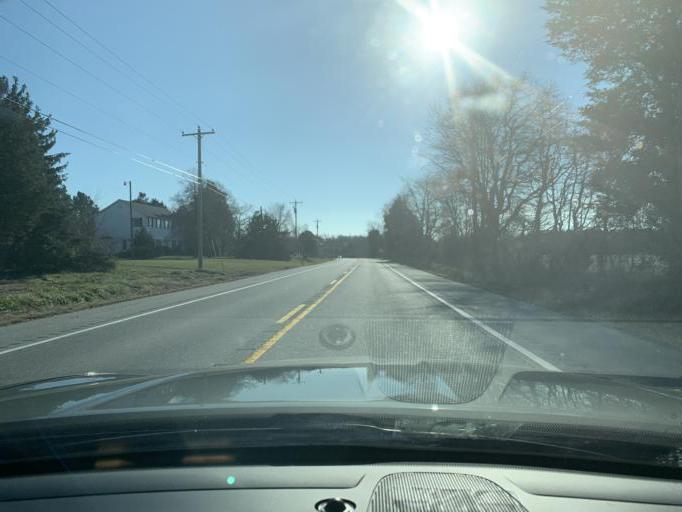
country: US
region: Maryland
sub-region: Queen Anne's County
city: Centreville
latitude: 39.1128
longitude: -76.0235
